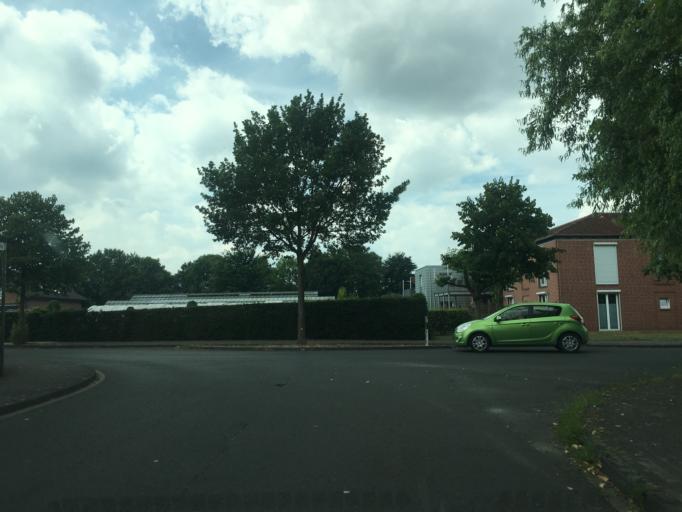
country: DE
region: North Rhine-Westphalia
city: Ludinghausen
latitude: 51.7735
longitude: 7.4588
